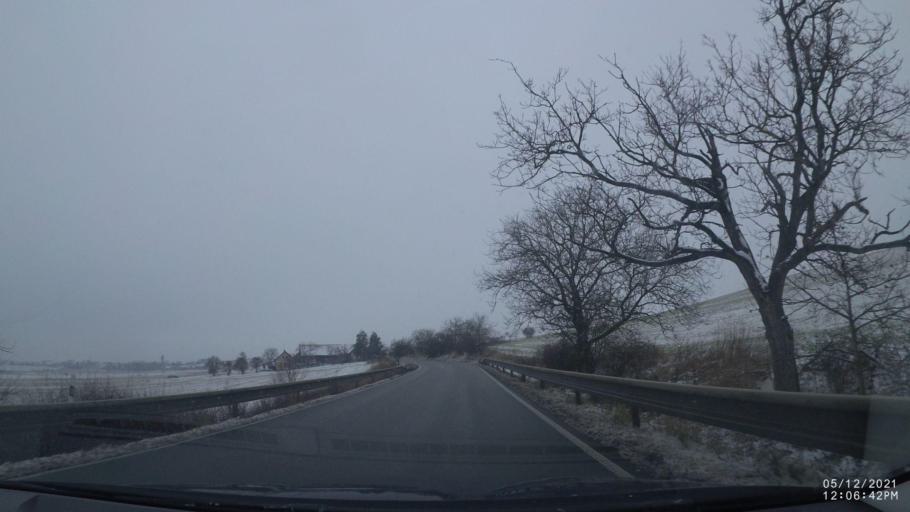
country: CZ
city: Ceske Mezirici
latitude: 50.2945
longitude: 16.0210
